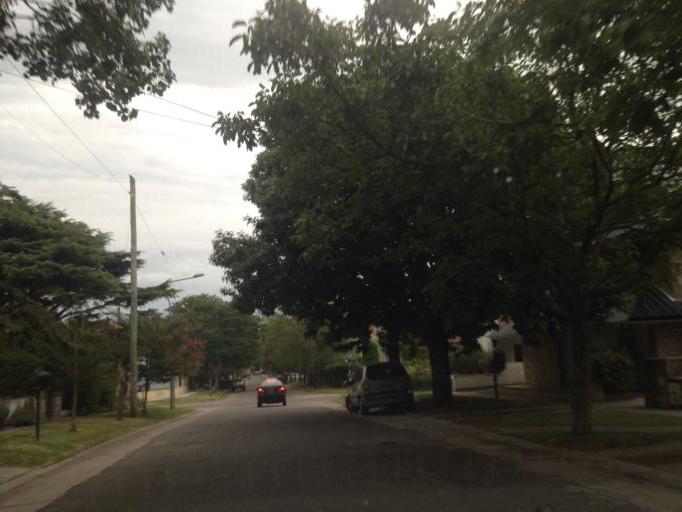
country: AR
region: Buenos Aires
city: Mar del Plata
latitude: -38.0232
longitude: -57.5399
